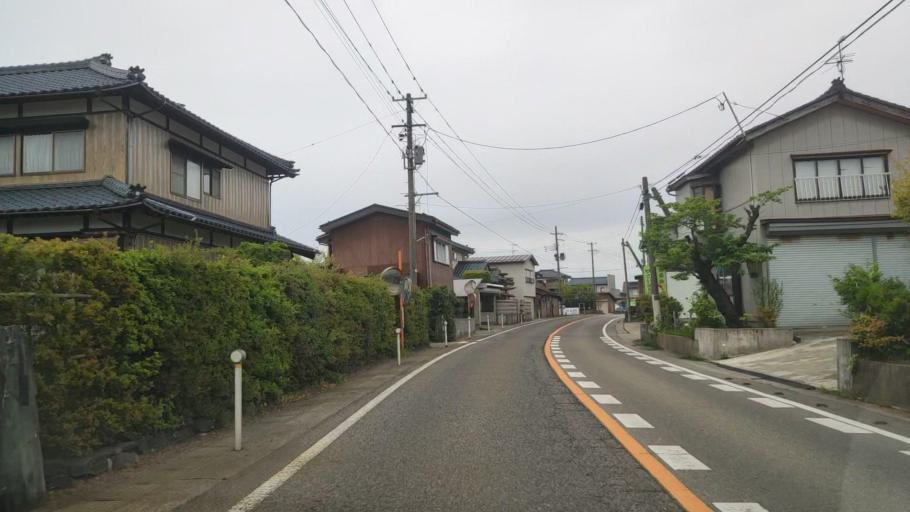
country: JP
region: Niigata
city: Kamo
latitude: 37.7158
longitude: 139.0733
